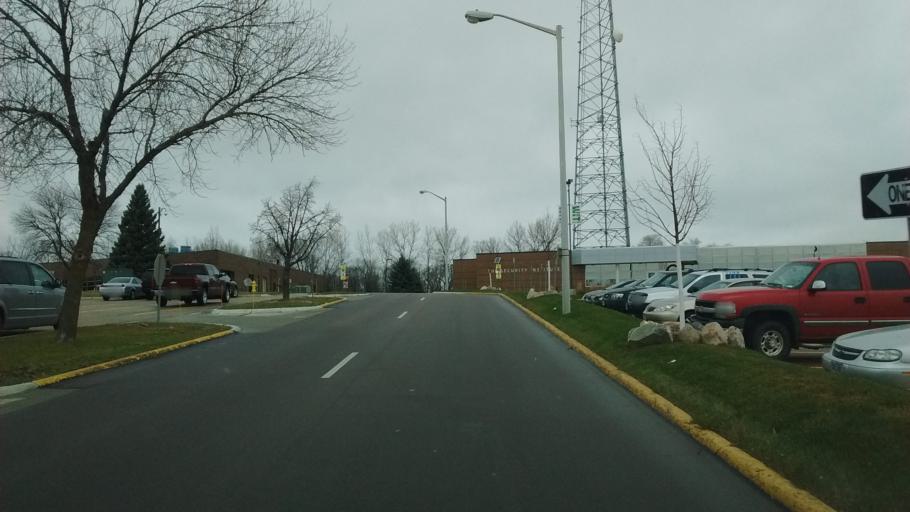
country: US
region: Iowa
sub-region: Woodbury County
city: Sioux City
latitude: 42.4850
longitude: -96.3466
